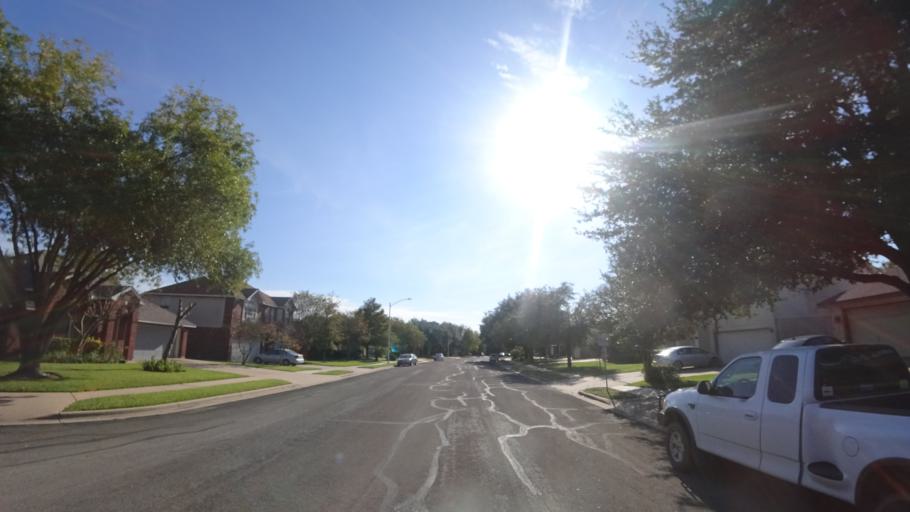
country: US
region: Texas
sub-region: Travis County
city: Pflugerville
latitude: 30.4070
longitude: -97.6494
